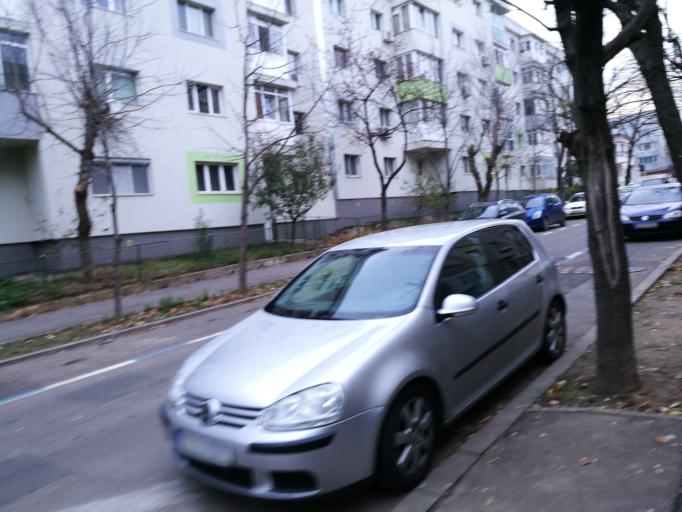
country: RO
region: Ilfov
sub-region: Comuna Otopeni
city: Otopeni
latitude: 44.4916
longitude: 26.0818
